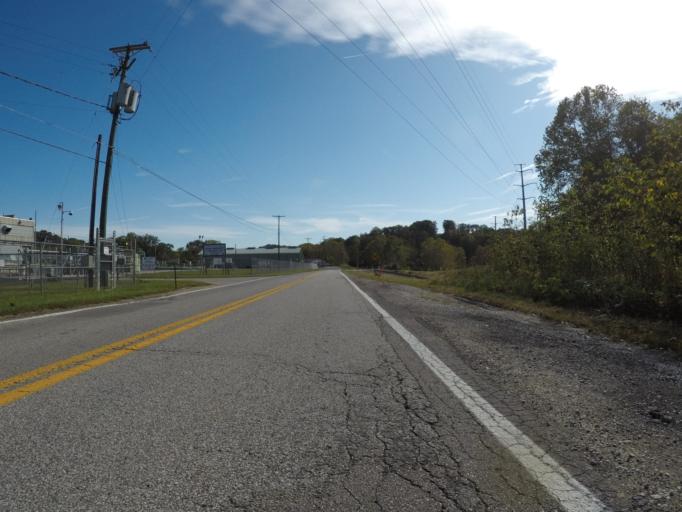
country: US
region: West Virginia
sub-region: Wayne County
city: Ceredo
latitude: 38.3670
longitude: -82.5330
